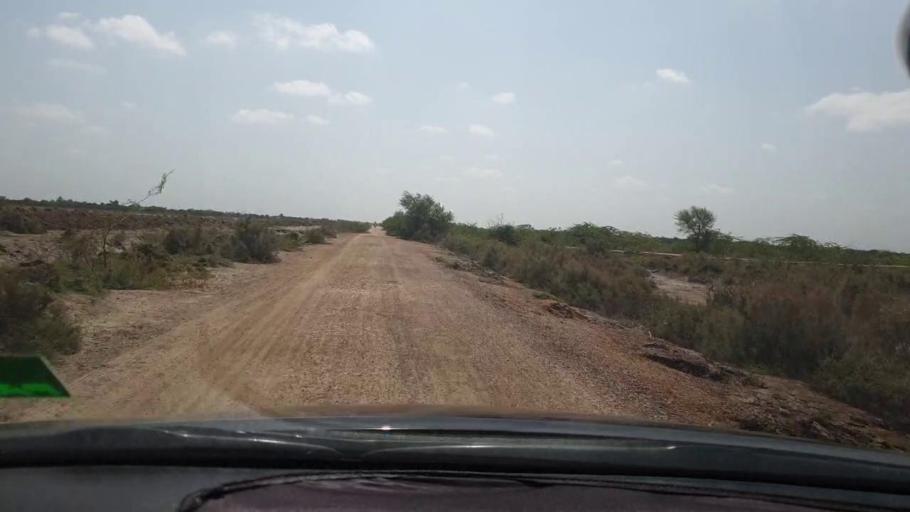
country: PK
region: Sindh
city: Tando Bago
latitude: 24.8320
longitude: 69.0567
